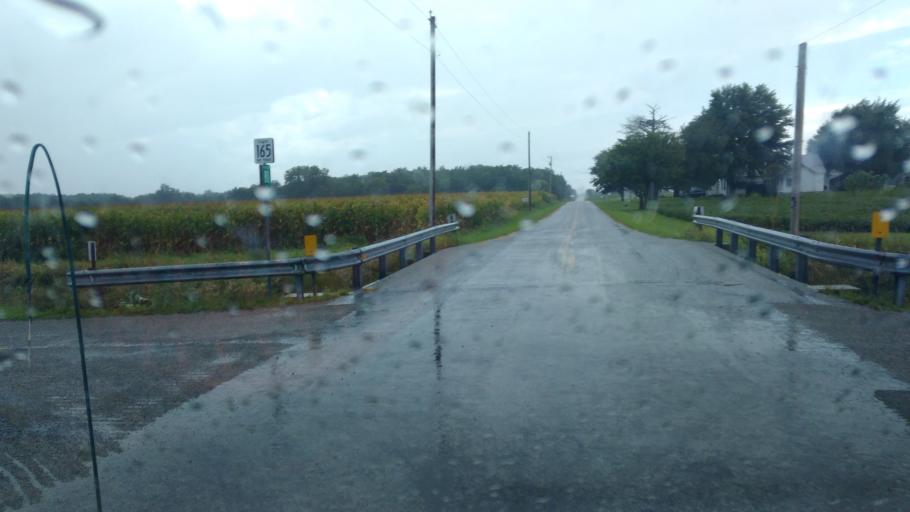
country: US
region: Ohio
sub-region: Hardin County
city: Kenton
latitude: 40.7175
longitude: -83.5949
